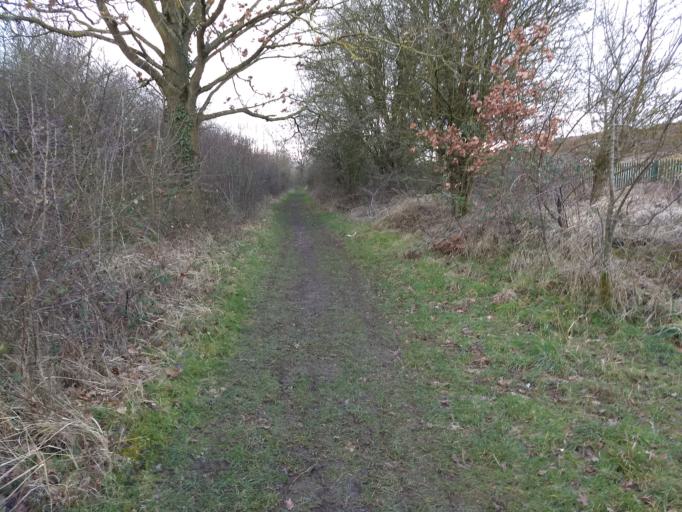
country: GB
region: England
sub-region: Buckinghamshire
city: Bletchley
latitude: 51.9866
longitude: -0.7400
